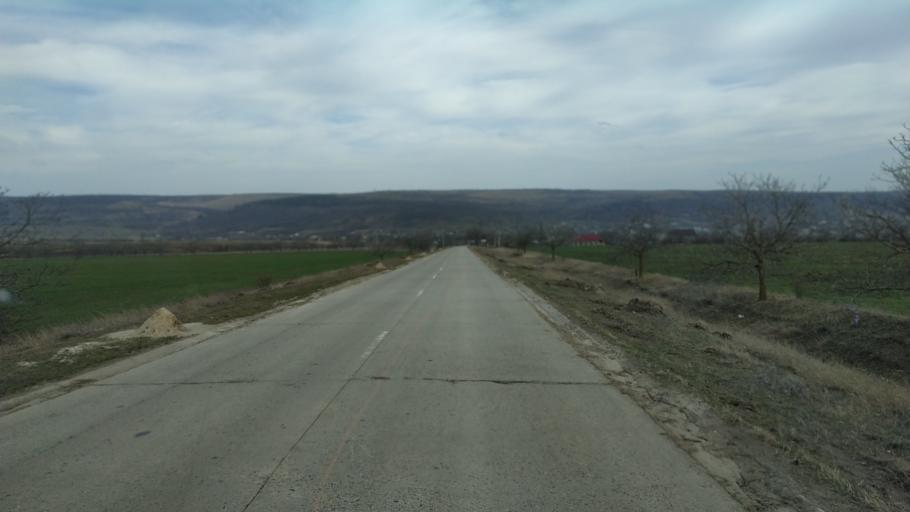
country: MD
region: Nisporeni
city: Nisporeni
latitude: 46.9294
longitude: 28.2514
